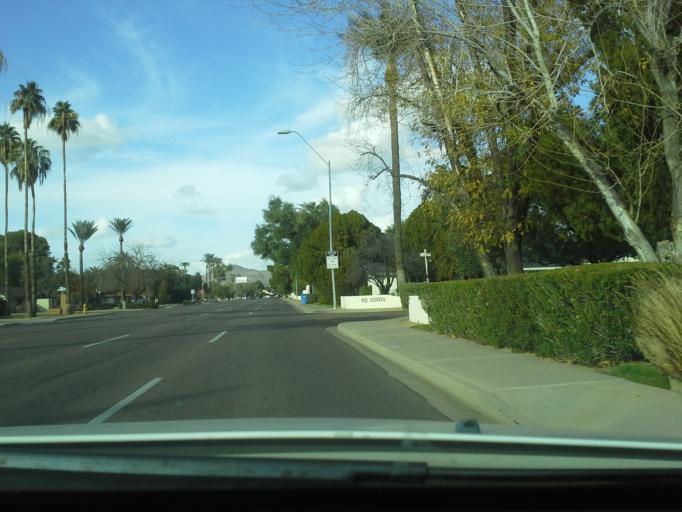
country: US
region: Arizona
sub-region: Maricopa County
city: Phoenix
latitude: 33.5458
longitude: -112.0824
